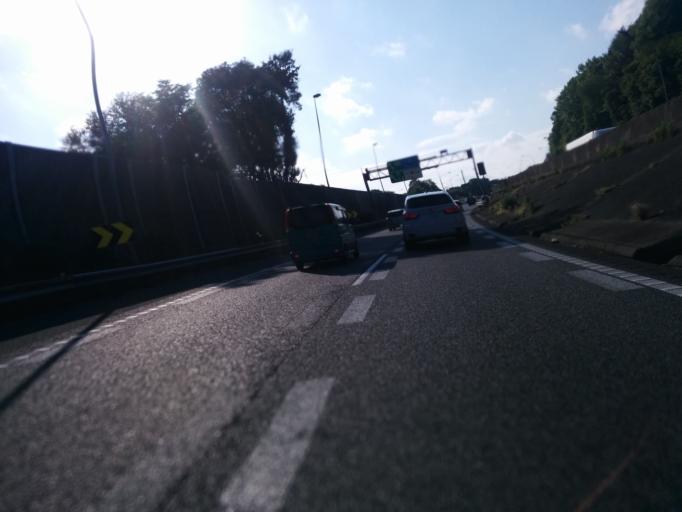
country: JP
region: Shiga Prefecture
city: Otsu-shi
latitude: 34.9987
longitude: 135.8651
